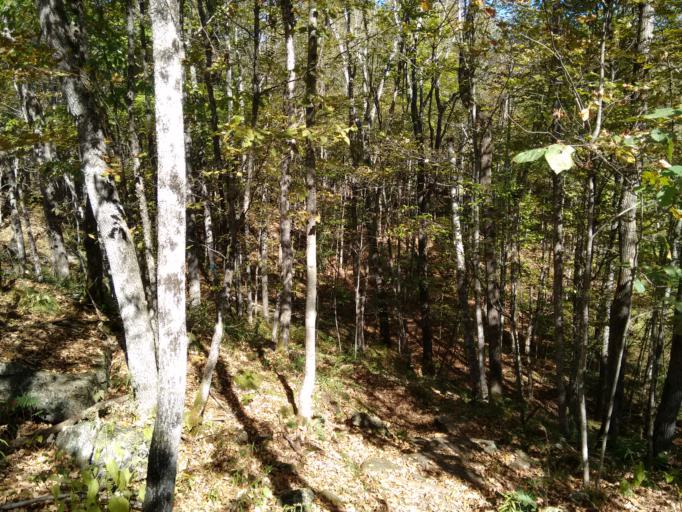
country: CA
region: Ontario
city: Kingston
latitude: 44.5061
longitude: -76.5530
